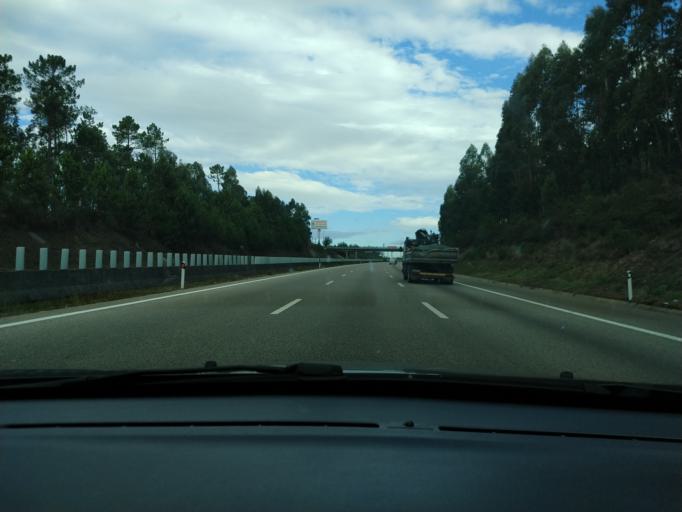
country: PT
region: Aveiro
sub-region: Santa Maria da Feira
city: Rio Meao
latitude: 40.9397
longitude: -8.5738
